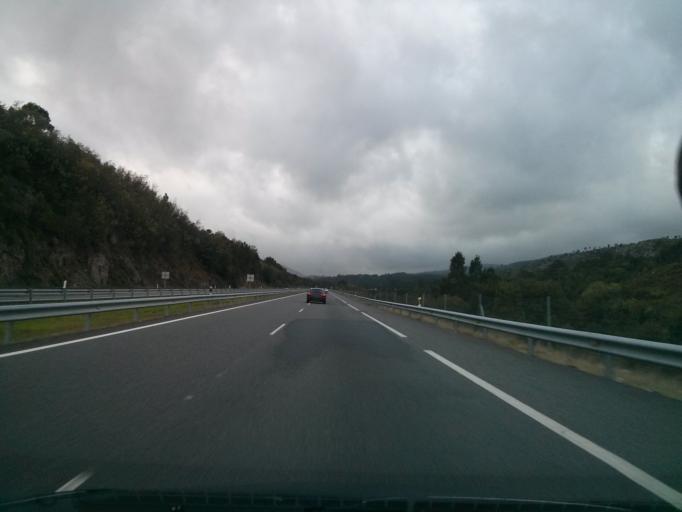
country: ES
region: Galicia
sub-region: Provincia de Ourense
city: Carballeda de Avia
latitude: 42.3077
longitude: -8.1758
